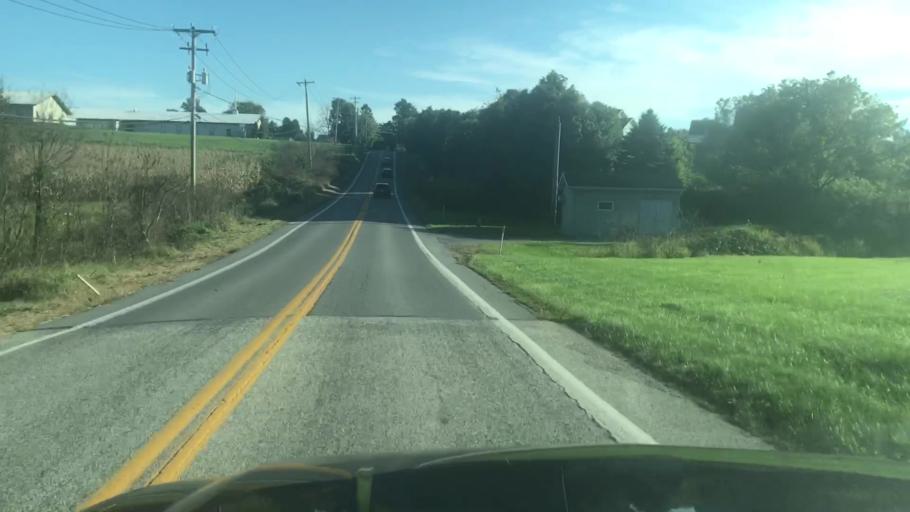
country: US
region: Pennsylvania
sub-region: Cumberland County
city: Enola
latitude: 40.2722
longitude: -76.9861
